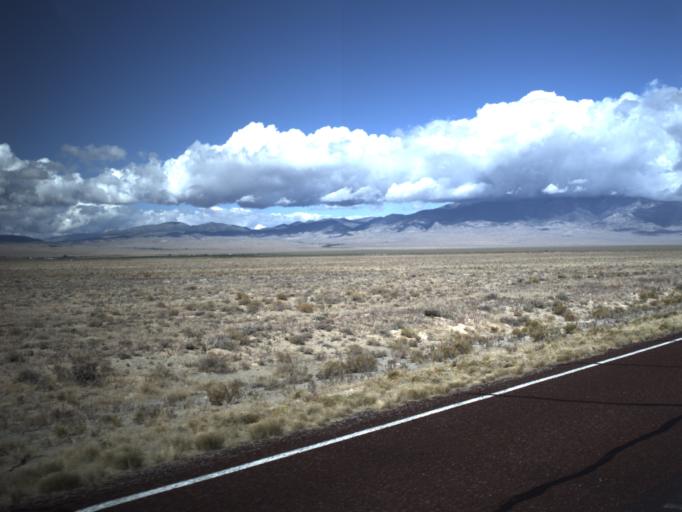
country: US
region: Nevada
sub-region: White Pine County
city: McGill
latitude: 38.9833
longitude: -114.0342
